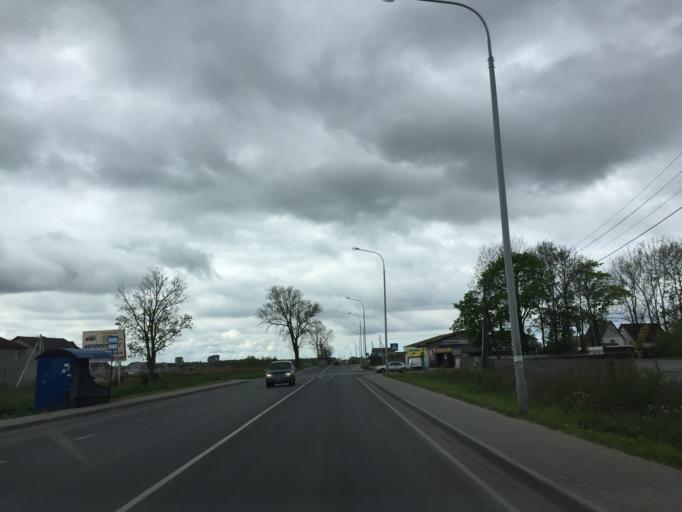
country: RU
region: Kaliningrad
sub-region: Gorod Kaliningrad
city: Kaliningrad
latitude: 54.6661
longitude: 20.4196
